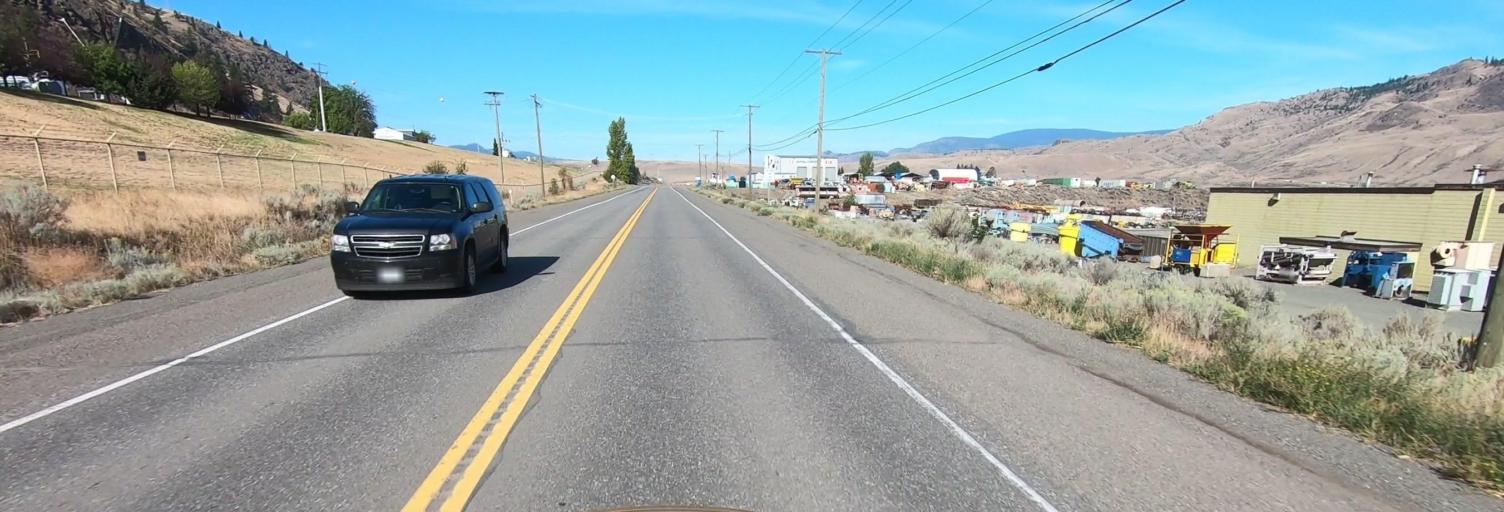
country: CA
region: British Columbia
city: Logan Lake
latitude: 50.7502
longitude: -120.8523
